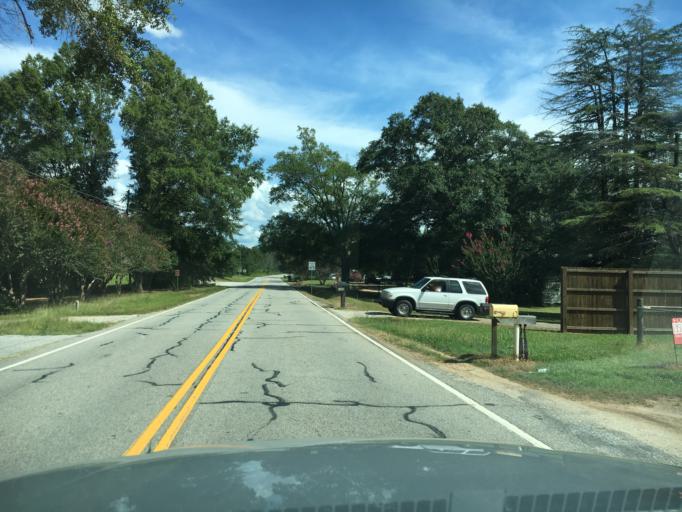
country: US
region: South Carolina
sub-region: Greenwood County
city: Ware Shoals
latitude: 34.4213
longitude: -82.2801
